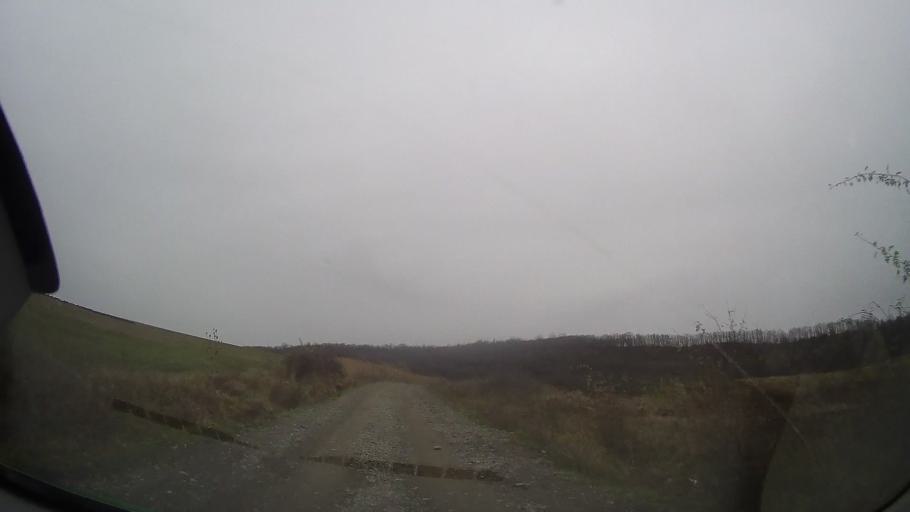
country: RO
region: Mures
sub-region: Comuna Ceausu de Campie
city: Ceausu de Campie
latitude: 46.6497
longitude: 24.4975
